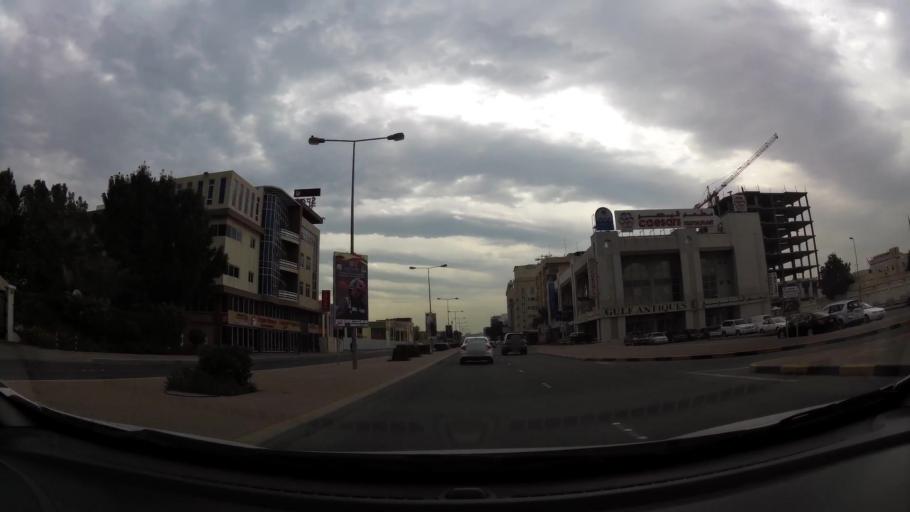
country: BH
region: Manama
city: Manama
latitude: 26.2142
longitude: 50.5899
